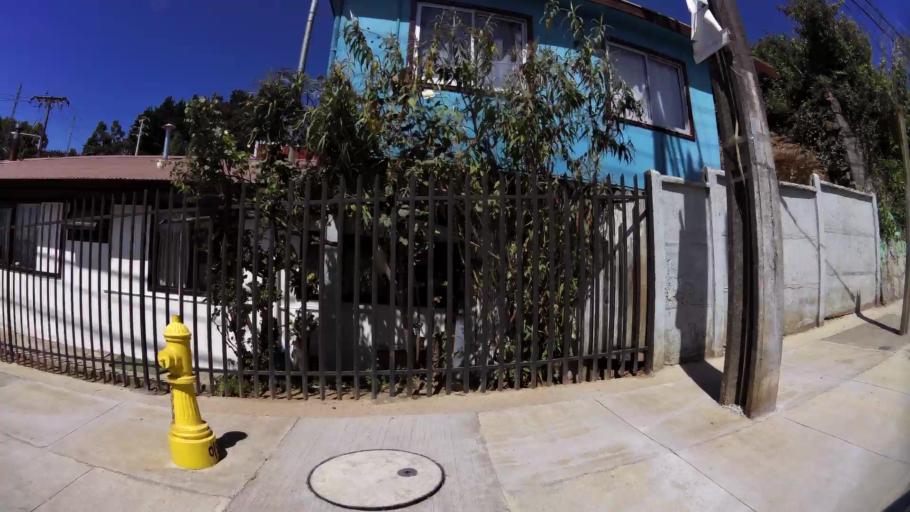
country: CL
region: Biobio
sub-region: Provincia de Concepcion
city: Penco
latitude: -36.7439
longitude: -72.9917
